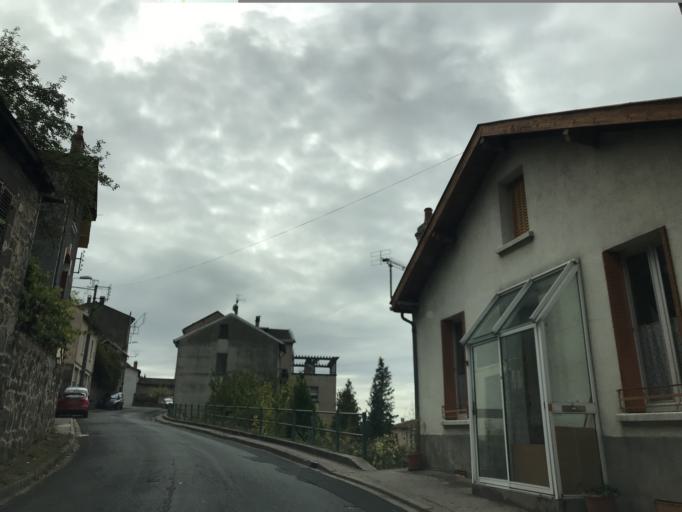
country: FR
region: Auvergne
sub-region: Departement du Puy-de-Dome
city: Thiers
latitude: 45.8551
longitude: 3.5529
